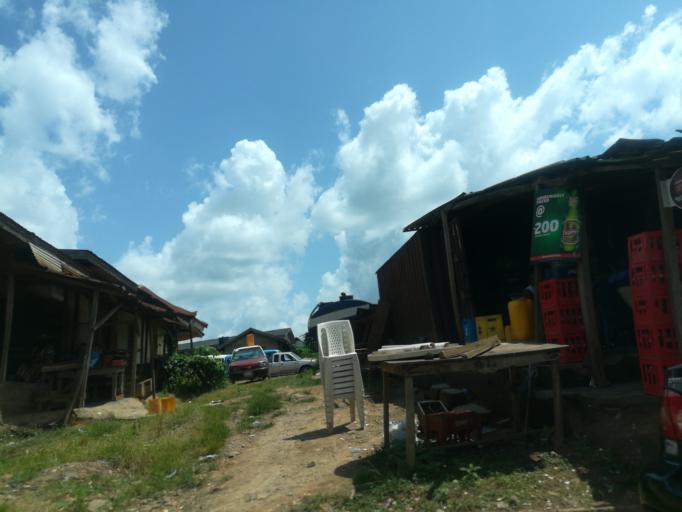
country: NG
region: Oyo
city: Egbeda
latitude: 7.4314
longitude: 4.0046
